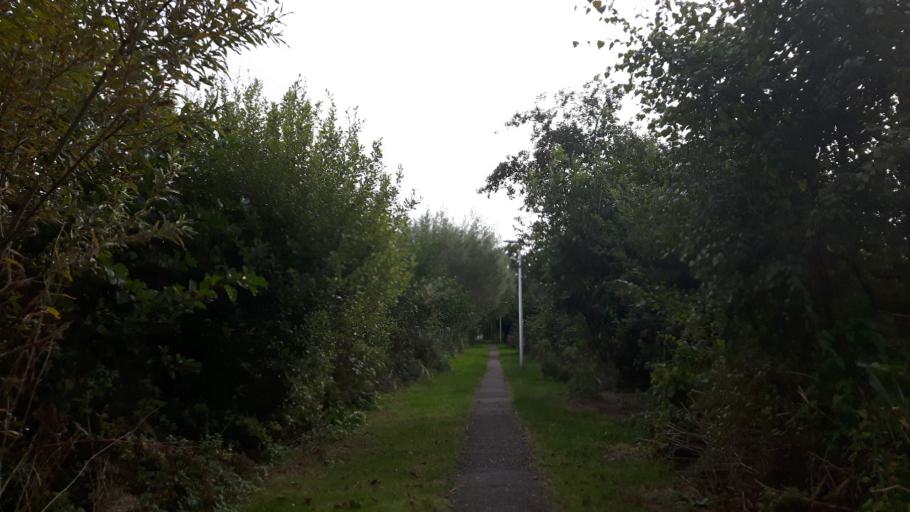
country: NL
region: Utrecht
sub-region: Gemeente De Ronde Venen
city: Mijdrecht
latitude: 52.1668
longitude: 4.8382
